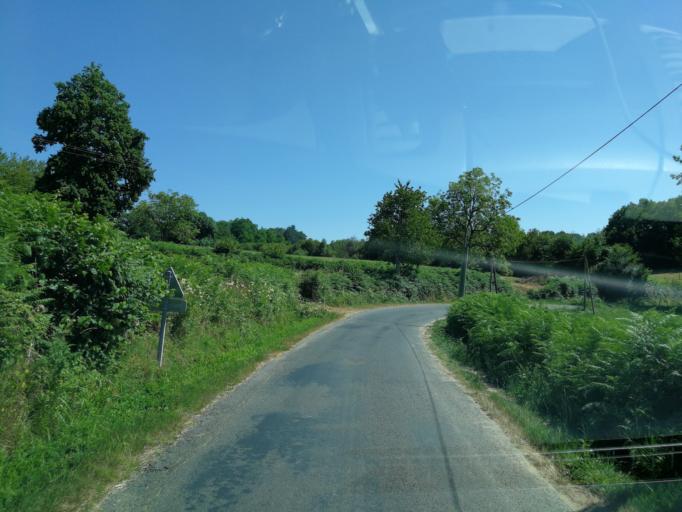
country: FR
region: Limousin
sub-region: Departement de la Correze
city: Sainte-Fereole
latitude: 45.2383
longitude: 1.5939
